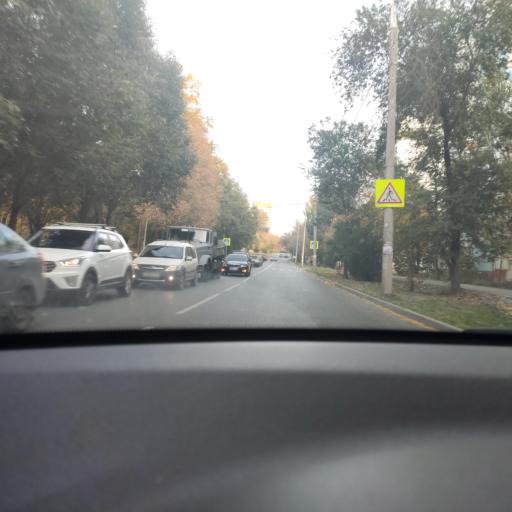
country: RU
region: Samara
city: Samara
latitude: 53.2028
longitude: 50.2212
